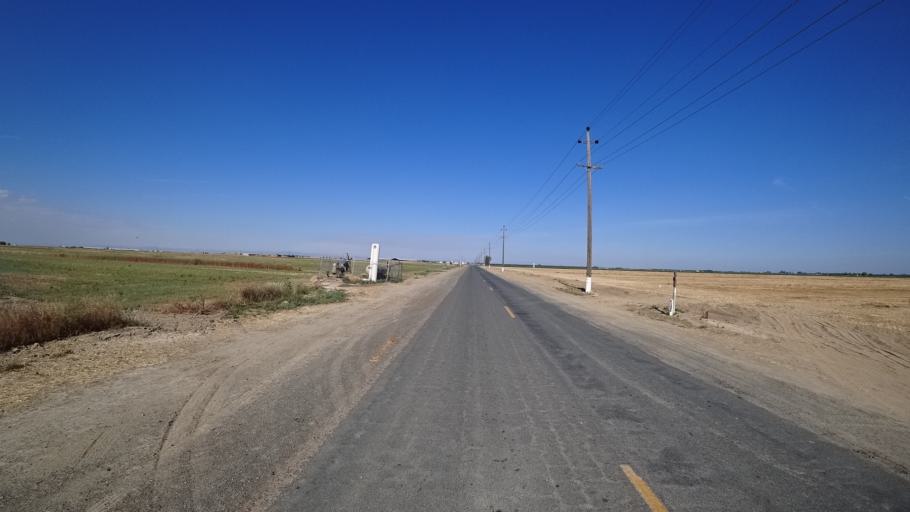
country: US
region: California
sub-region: Kings County
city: Home Garden
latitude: 36.2258
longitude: -119.6748
